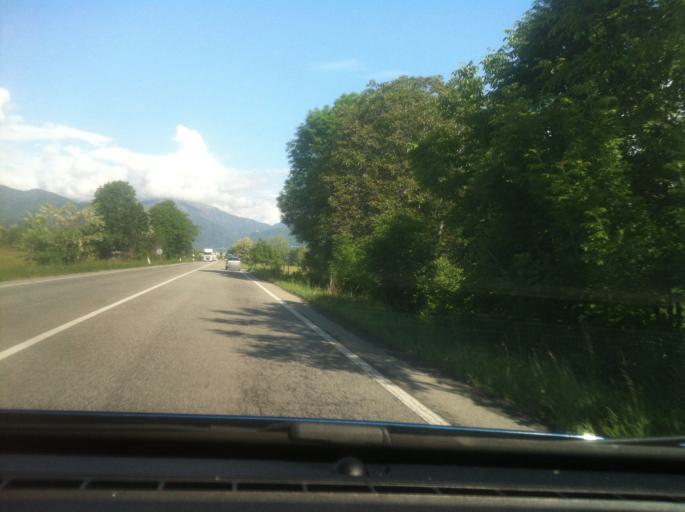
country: IT
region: Piedmont
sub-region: Provincia di Torino
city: Salassa
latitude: 45.3626
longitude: 7.6879
